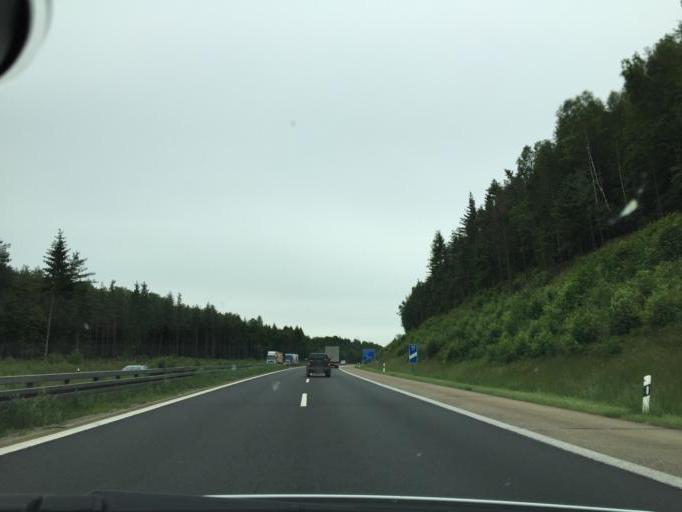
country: DE
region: Bavaria
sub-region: Regierungsbezirk Unterfranken
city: Bad Bruckenau
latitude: 50.3408
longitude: 9.7669
